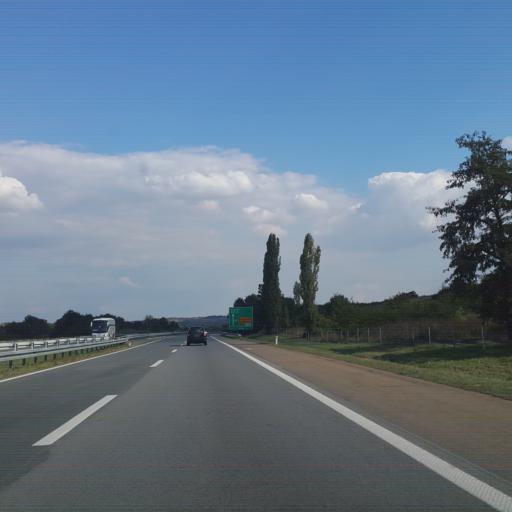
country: RS
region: Central Serbia
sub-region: Podunavski Okrug
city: Smederevo
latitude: 44.5798
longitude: 20.8785
